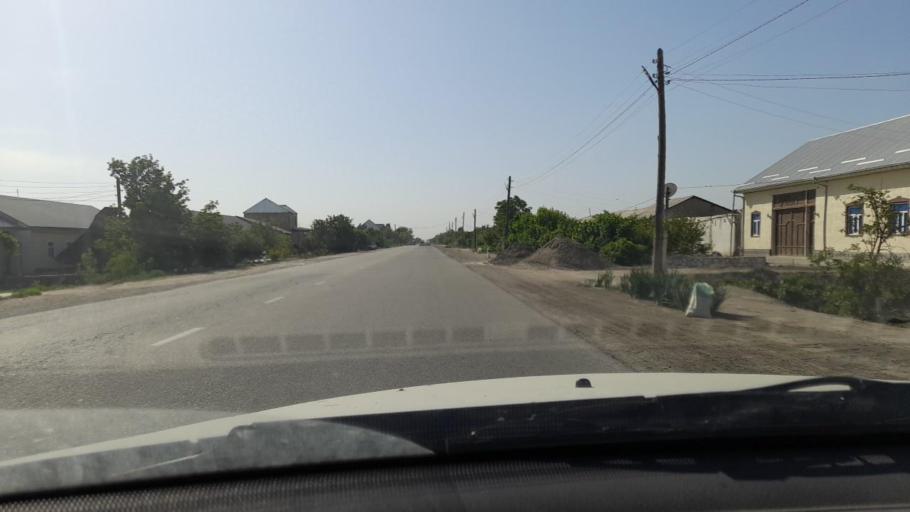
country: UZ
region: Bukhara
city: Romiton
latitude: 39.9046
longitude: 64.4023
